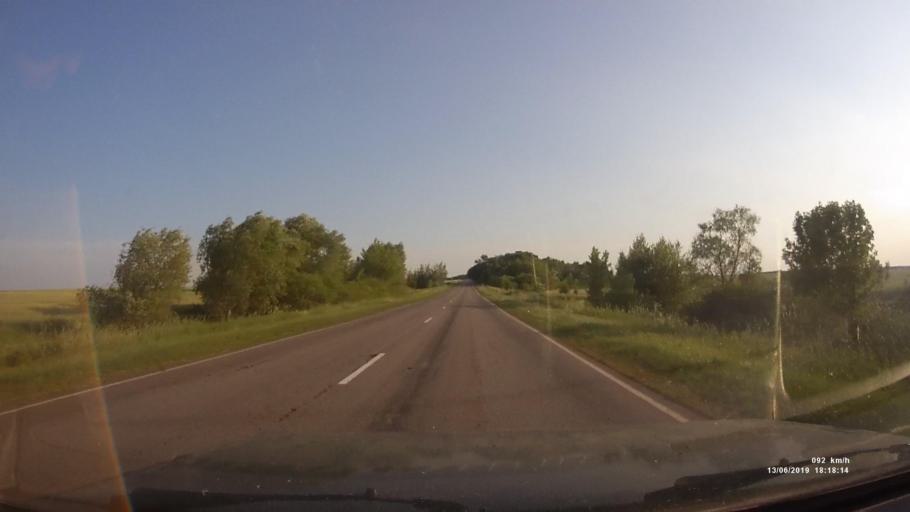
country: RU
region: Rostov
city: Kazanskaya
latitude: 49.9104
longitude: 41.3162
